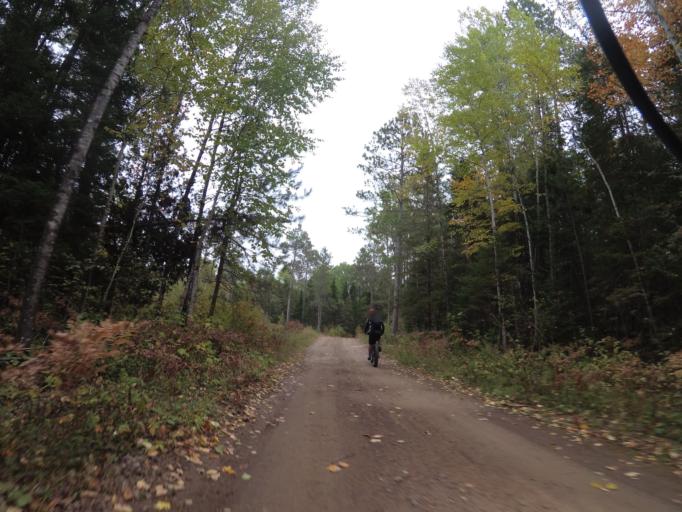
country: CA
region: Ontario
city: Renfrew
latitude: 45.2134
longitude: -77.1245
